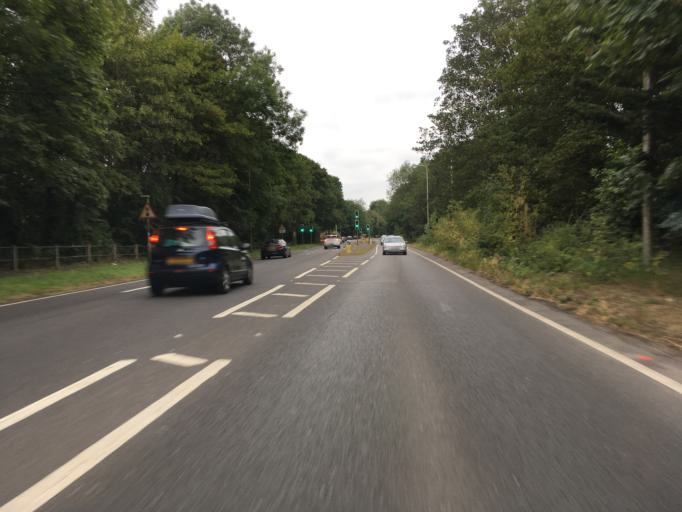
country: GB
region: England
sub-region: Hertfordshire
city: Markyate
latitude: 51.8386
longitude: -0.4614
